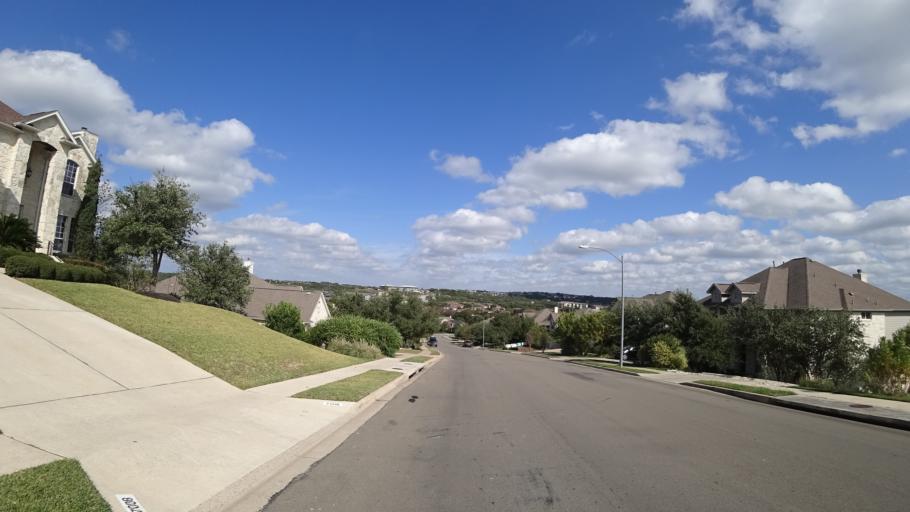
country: US
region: Texas
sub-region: Travis County
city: Barton Creek
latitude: 30.2451
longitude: -97.8975
